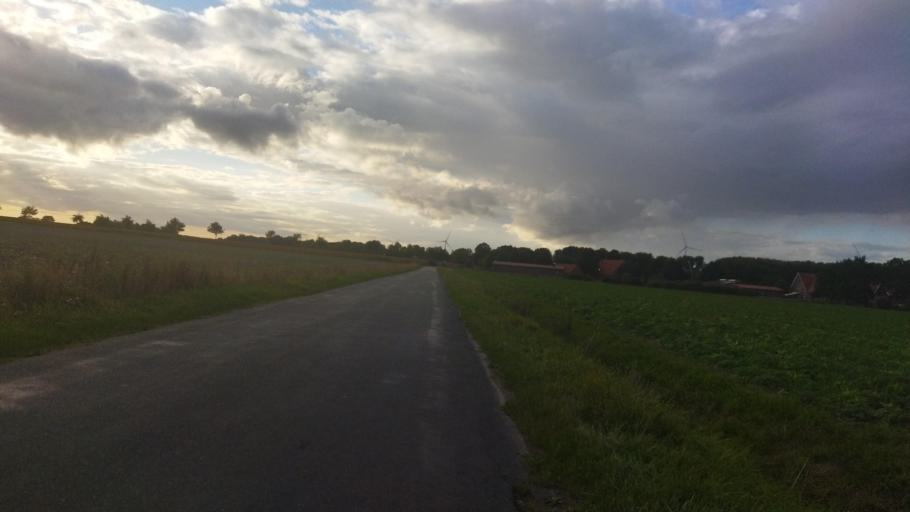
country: DE
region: North Rhine-Westphalia
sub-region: Regierungsbezirk Munster
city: Billerbeck
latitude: 51.9799
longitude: 7.2325
